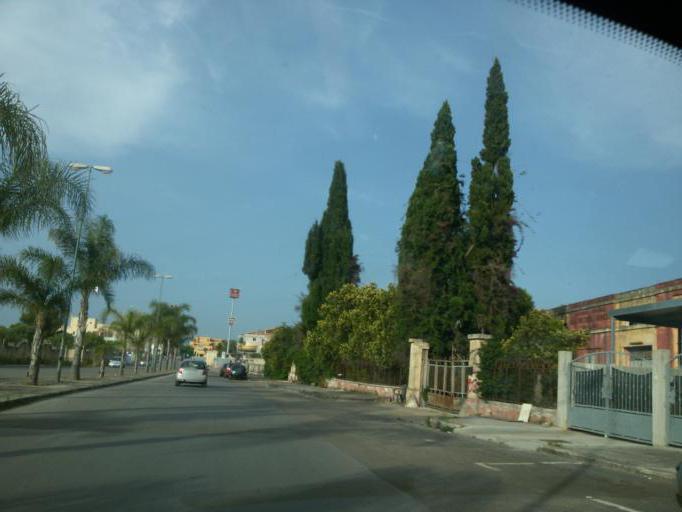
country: IT
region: Apulia
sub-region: Provincia di Brindisi
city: Cellino San Marco
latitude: 40.4747
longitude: 17.9725
